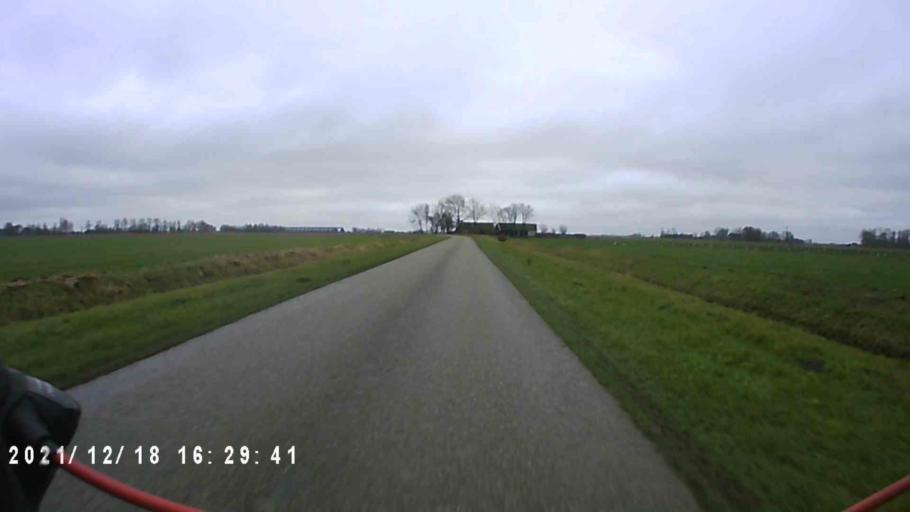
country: NL
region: Friesland
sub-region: Gemeente Dongeradeel
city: Dokkum
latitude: 53.3624
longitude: 6.0356
